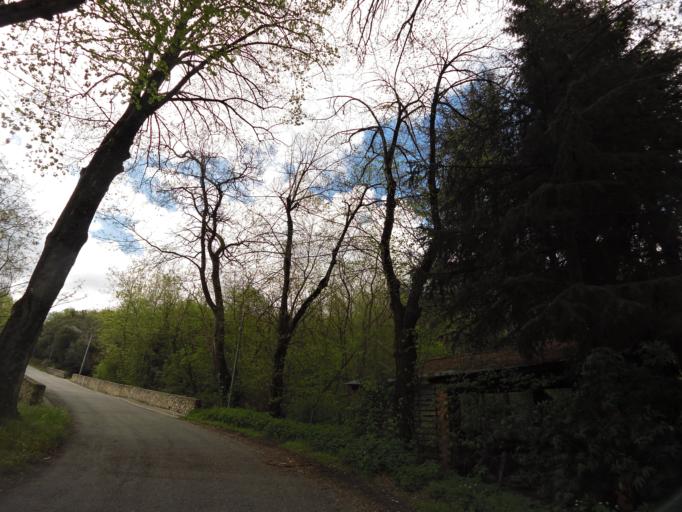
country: FR
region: Languedoc-Roussillon
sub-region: Departement de l'Aude
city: Villepinte
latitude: 43.3540
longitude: 2.1218
